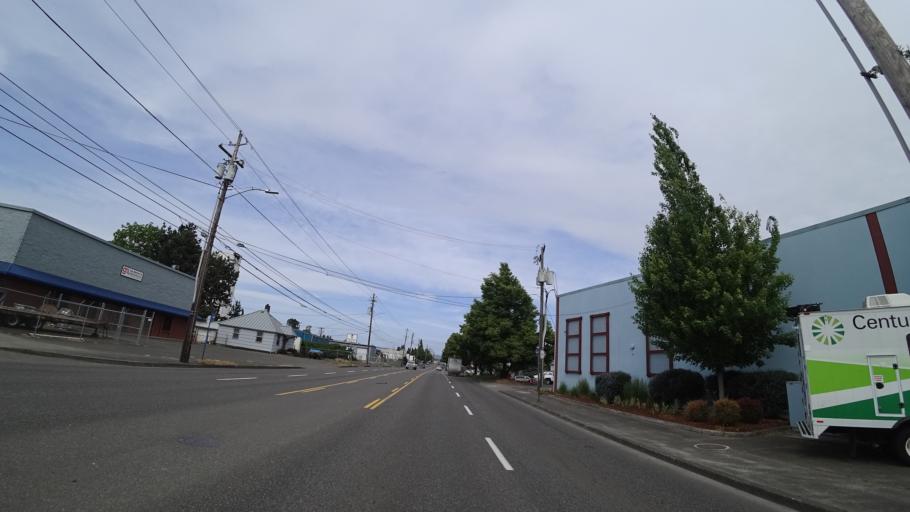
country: US
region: Oregon
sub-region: Multnomah County
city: Portland
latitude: 45.5753
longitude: -122.6379
